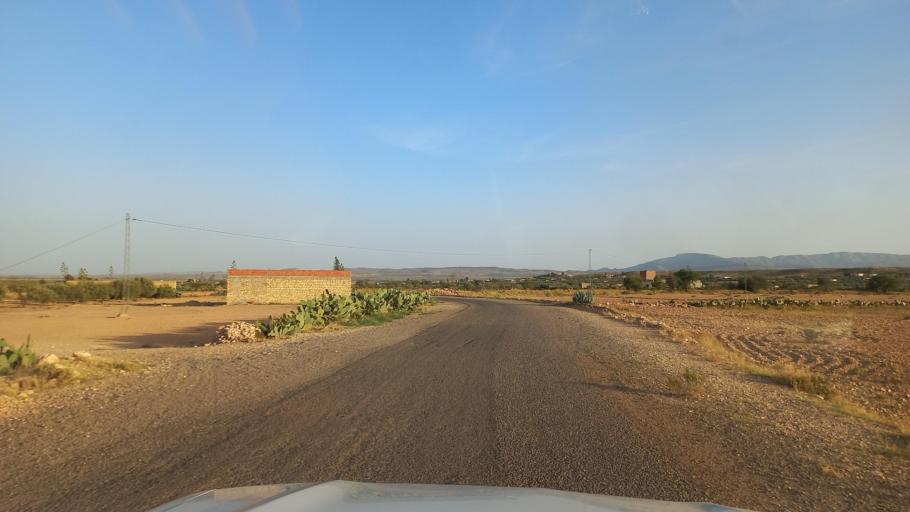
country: TN
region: Al Qasrayn
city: Kasserine
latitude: 35.2712
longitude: 8.9283
